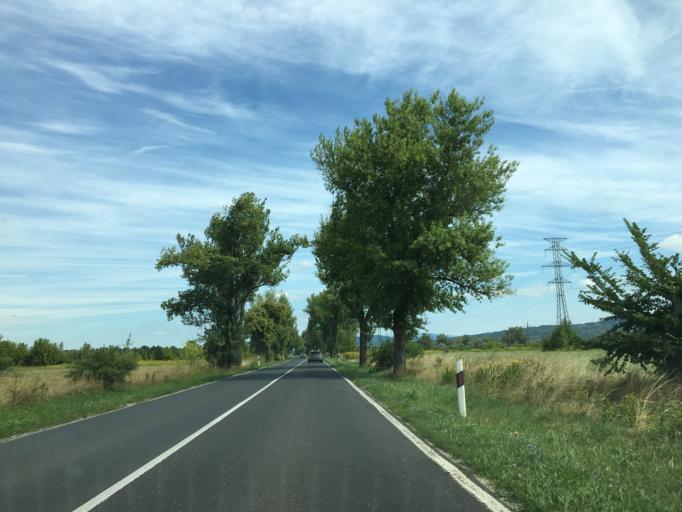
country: SK
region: Nitriansky
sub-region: Okres Nove Zamky
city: Sturovo
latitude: 47.7572
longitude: 18.6973
